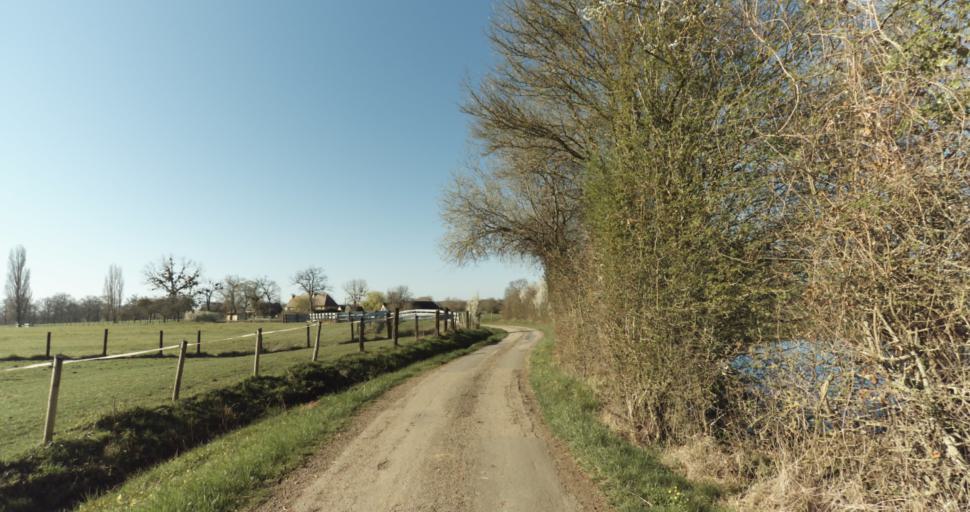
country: FR
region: Lower Normandy
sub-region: Departement du Calvados
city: Saint-Pierre-sur-Dives
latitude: 48.9596
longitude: 0.0188
